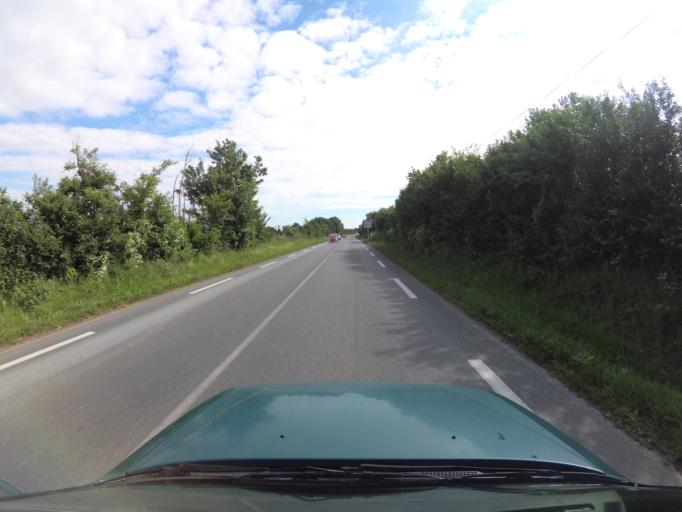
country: FR
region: Poitou-Charentes
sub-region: Departement de la Charente-Maritime
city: Saint-Xandre
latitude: 46.2222
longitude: -1.0855
